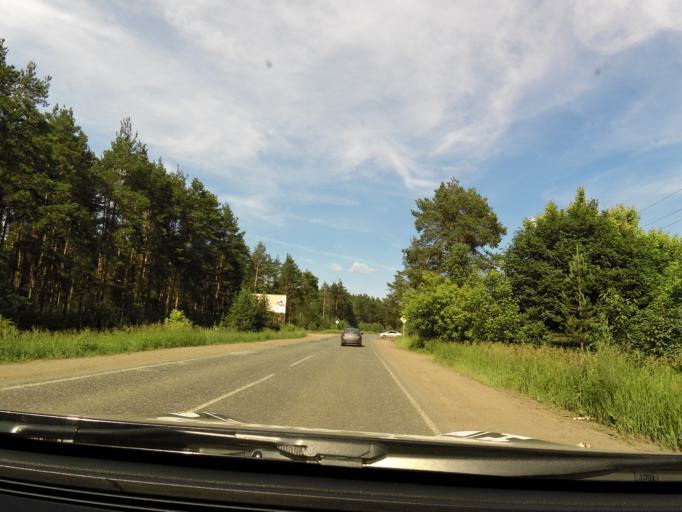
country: RU
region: Kirov
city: Belaya Kholunitsa
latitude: 58.8518
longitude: 50.8308
